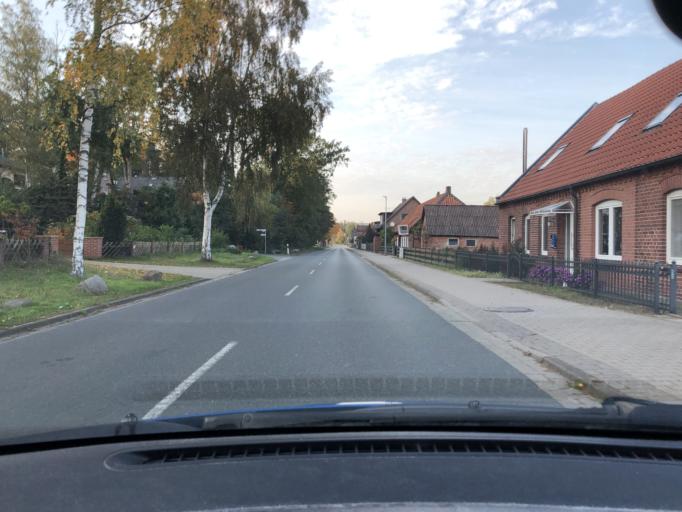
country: DE
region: Lower Saxony
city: Hitzacker
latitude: 53.1385
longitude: 11.0456
